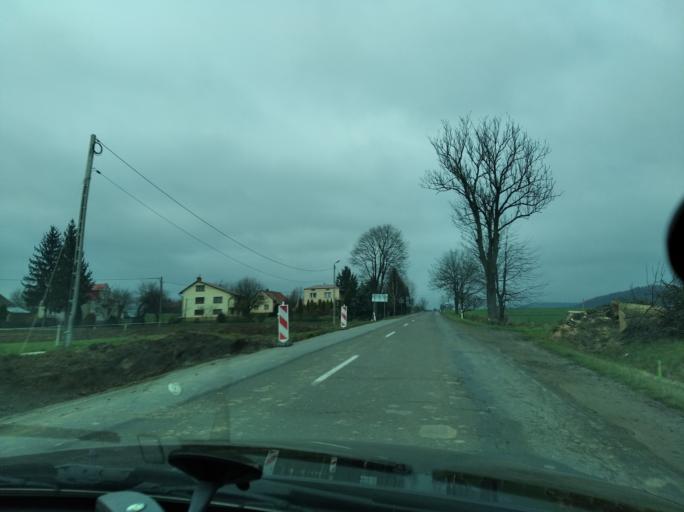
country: PL
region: Subcarpathian Voivodeship
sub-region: Powiat rzeszowski
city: Dynow
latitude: 49.8368
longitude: 22.2434
